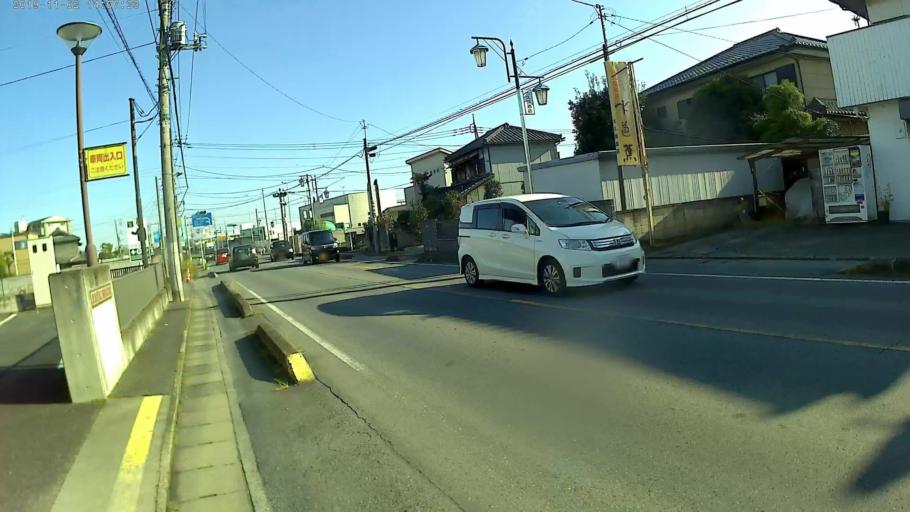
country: JP
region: Gunma
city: Takasaki
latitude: 36.3328
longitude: 138.9864
